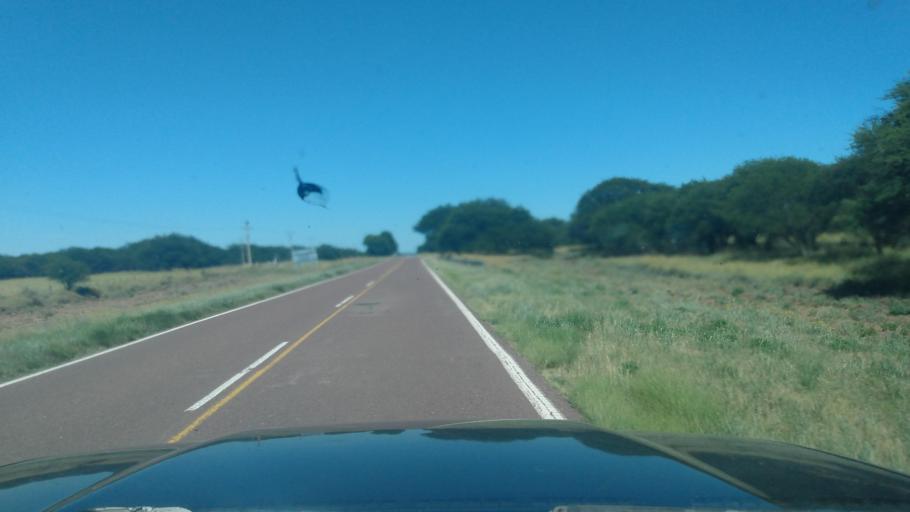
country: AR
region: La Pampa
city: General Acha
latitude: -37.4173
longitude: -64.8519
